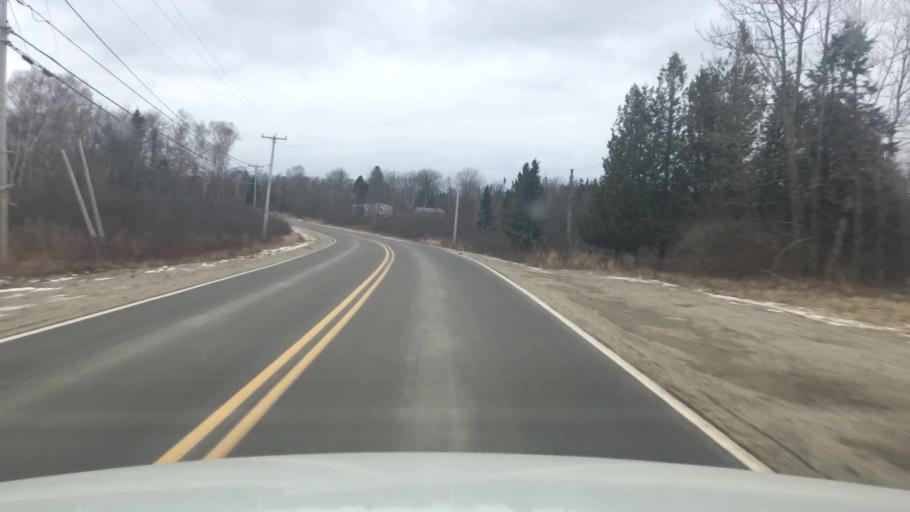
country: US
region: Maine
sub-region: Washington County
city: Jonesport
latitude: 44.5562
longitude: -67.6264
